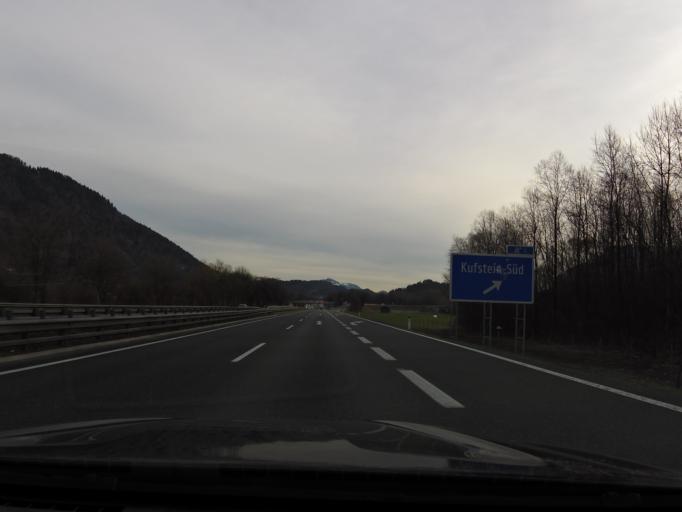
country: AT
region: Tyrol
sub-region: Politischer Bezirk Kufstein
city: Schwoich
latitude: 47.5647
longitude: 12.1388
